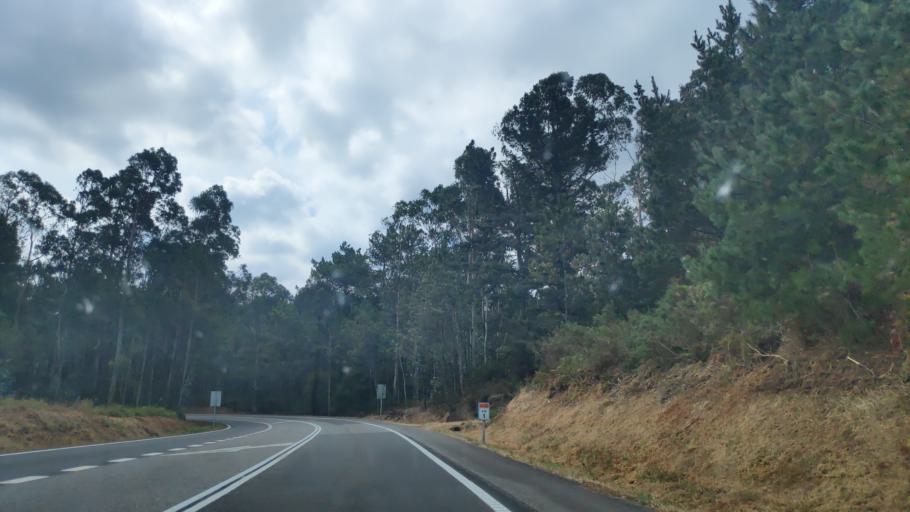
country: ES
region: Galicia
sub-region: Provincia de Pontevedra
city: Catoira
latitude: 42.6780
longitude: -8.7342
